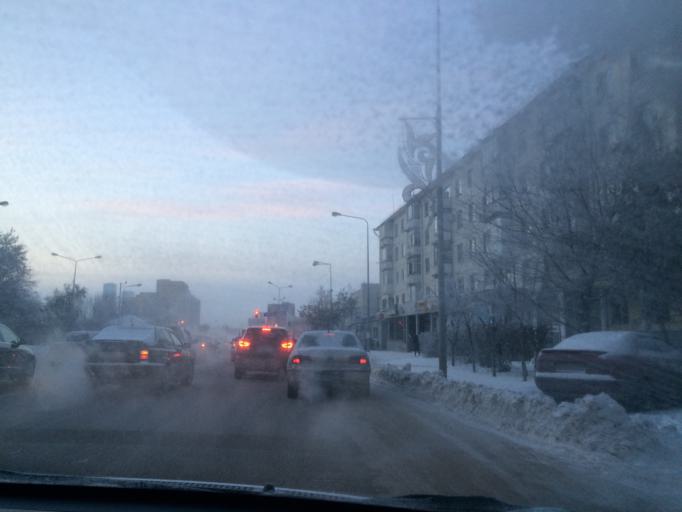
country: KZ
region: Astana Qalasy
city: Astana
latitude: 51.1770
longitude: 71.4106
